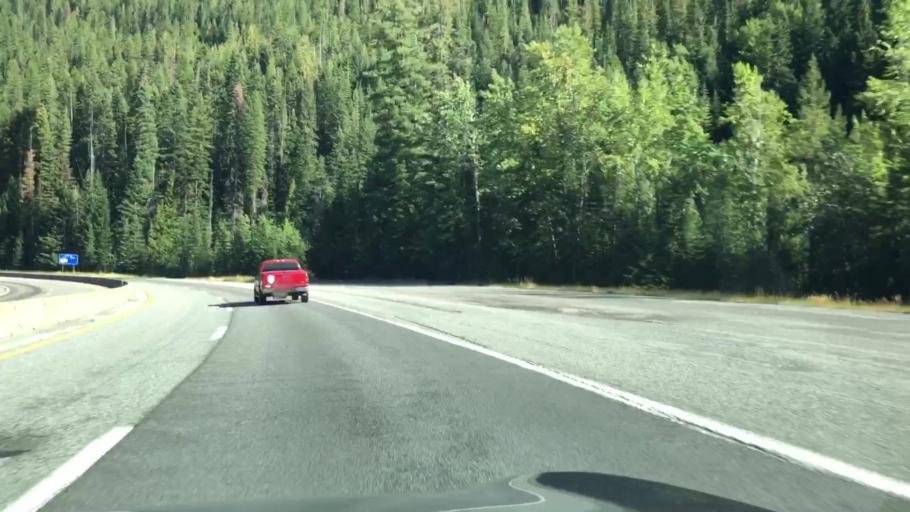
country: US
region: Idaho
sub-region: Shoshone County
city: Wallace
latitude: 47.4633
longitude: -115.8085
